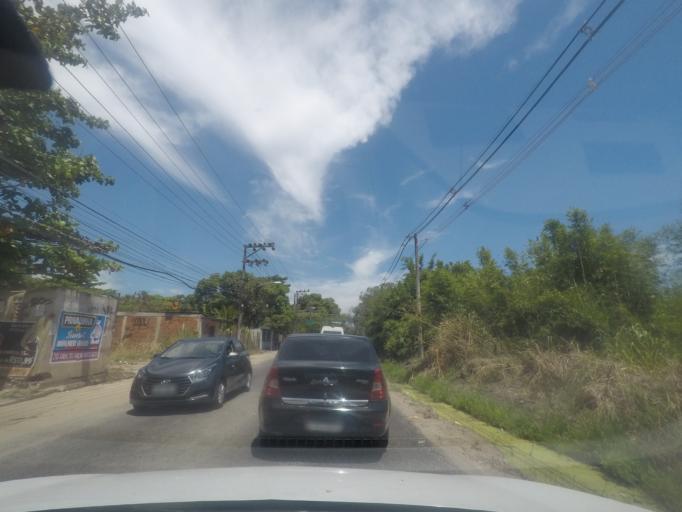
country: BR
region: Rio de Janeiro
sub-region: Itaguai
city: Itaguai
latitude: -22.9877
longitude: -43.6526
